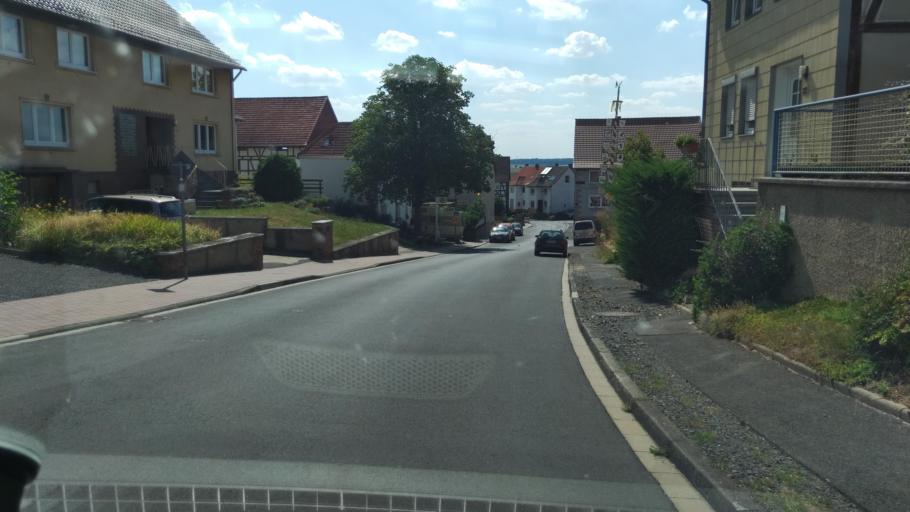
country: DE
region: Hesse
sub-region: Regierungsbezirk Kassel
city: Guxhagen
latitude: 51.1855
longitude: 9.4679
